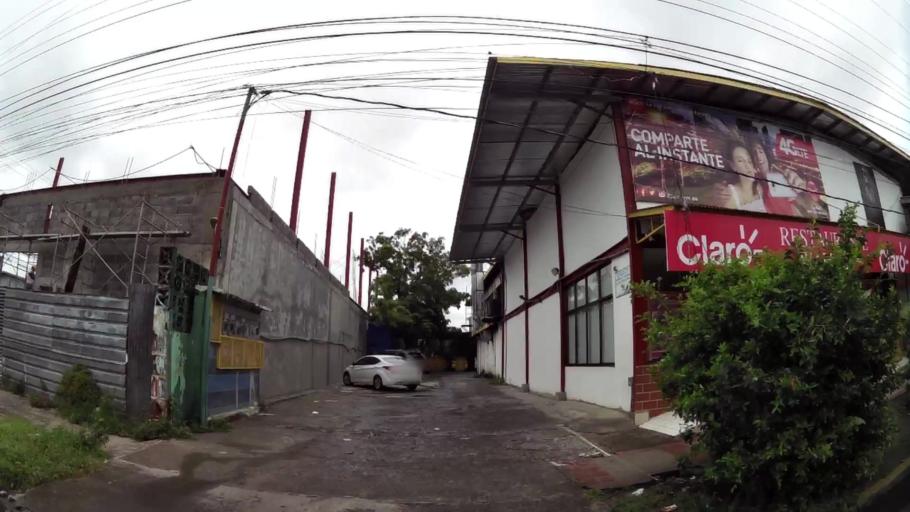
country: PA
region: Chiriqui
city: David
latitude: 8.4282
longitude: -82.4272
